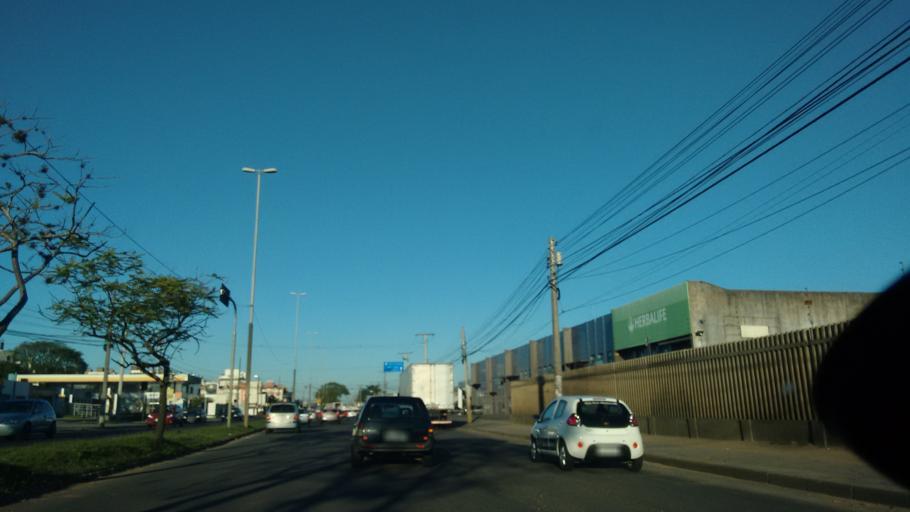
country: BR
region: Rio Grande do Sul
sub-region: Cachoeirinha
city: Cachoeirinha
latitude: -29.9979
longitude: -51.1446
